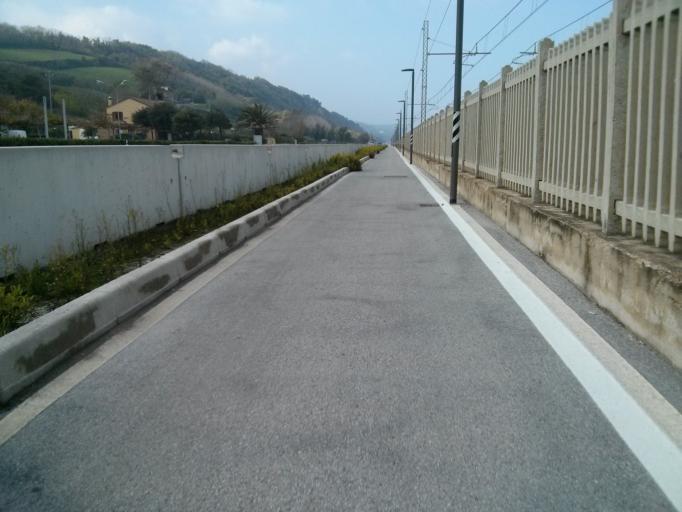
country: IT
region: The Marches
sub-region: Provincia di Pesaro e Urbino
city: Fenile
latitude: 43.8690
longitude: 12.9801
